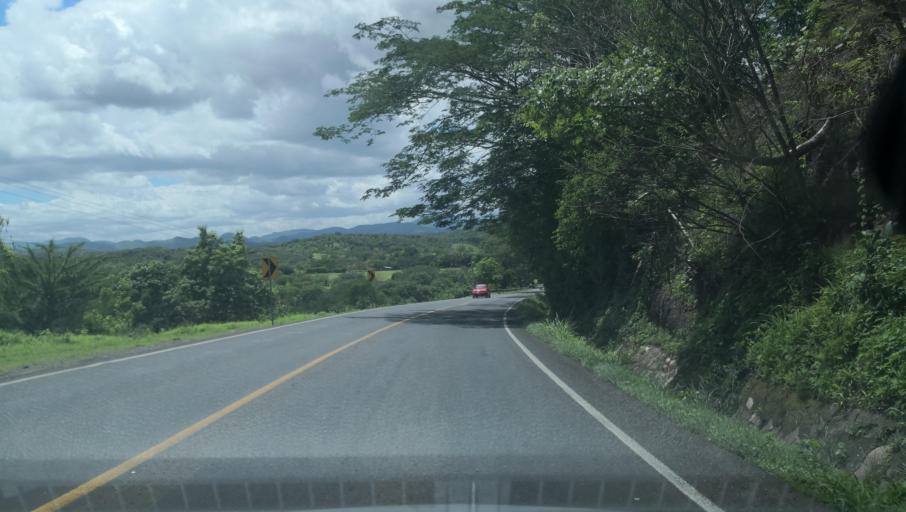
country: NI
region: Esteli
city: Condega
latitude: 13.4013
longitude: -86.3996
